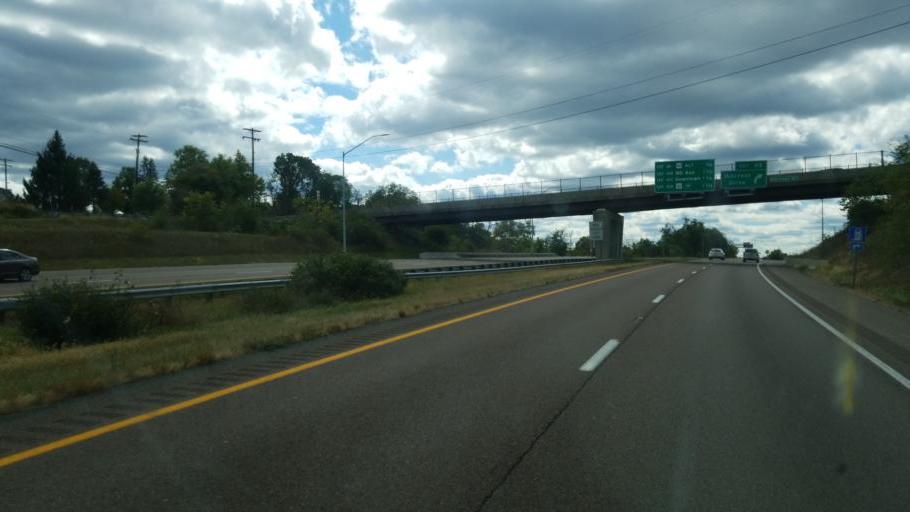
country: US
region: Maryland
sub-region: Allegany County
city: Cumberland
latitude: 39.6675
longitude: -78.7361
